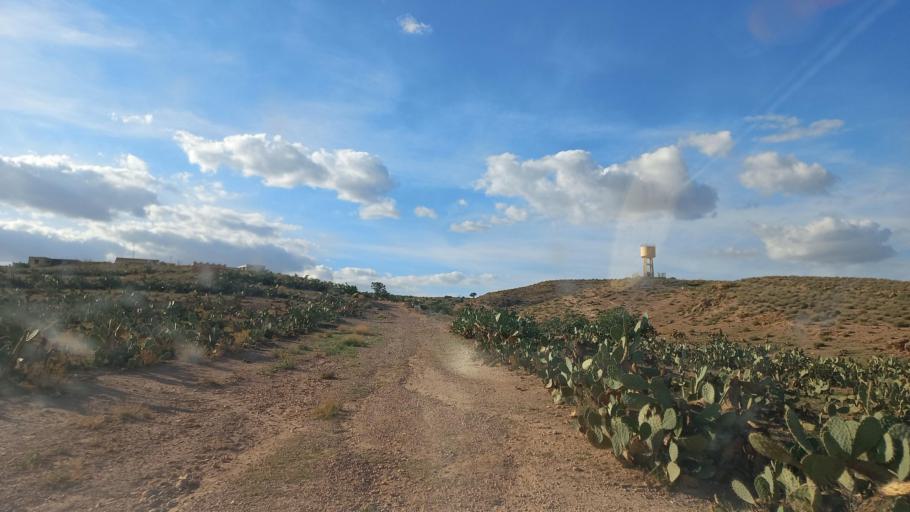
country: TN
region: Al Qasrayn
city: Sbiba
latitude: 35.3817
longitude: 9.0207
